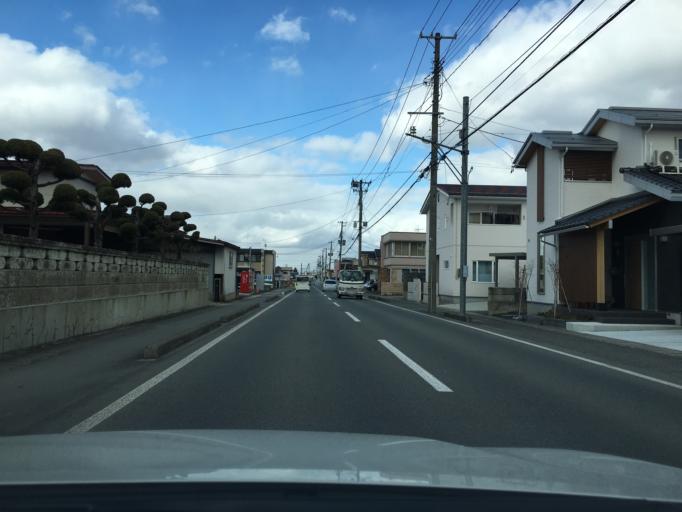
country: JP
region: Yamagata
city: Yamagata-shi
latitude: 38.2488
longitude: 140.3136
